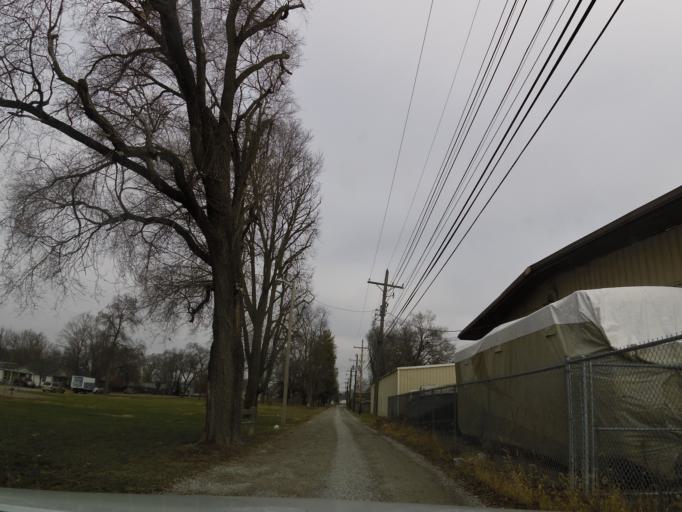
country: US
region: Indiana
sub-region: Bartholomew County
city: Columbus
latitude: 39.1932
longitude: -85.9014
